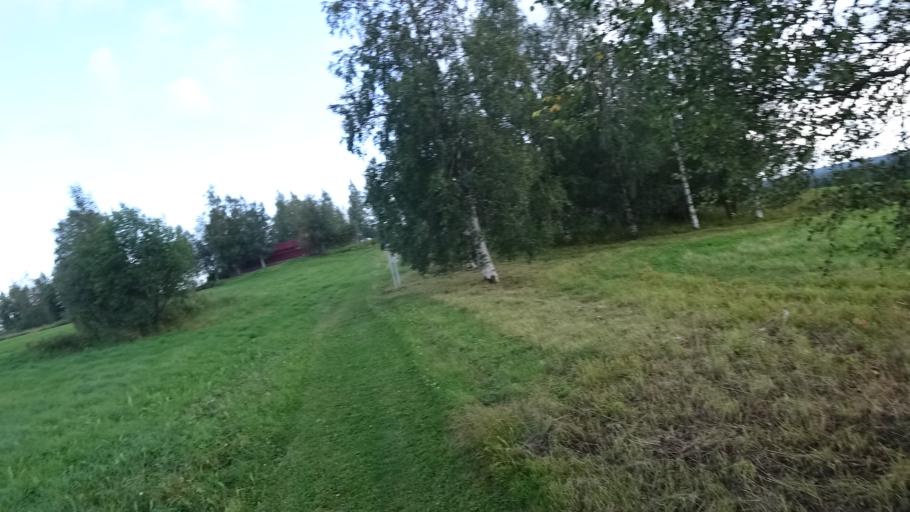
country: FI
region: North Karelia
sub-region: Joensuu
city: Ilomantsi
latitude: 62.6731
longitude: 30.9177
